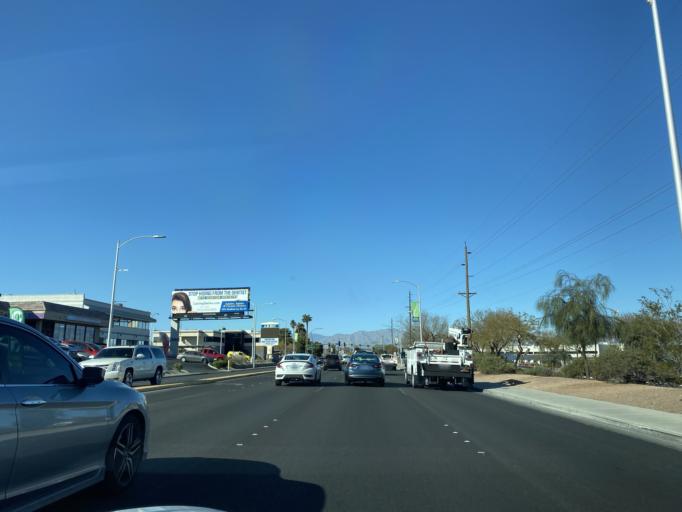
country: US
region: Nevada
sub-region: Clark County
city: Las Vegas
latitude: 36.1610
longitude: -115.1925
